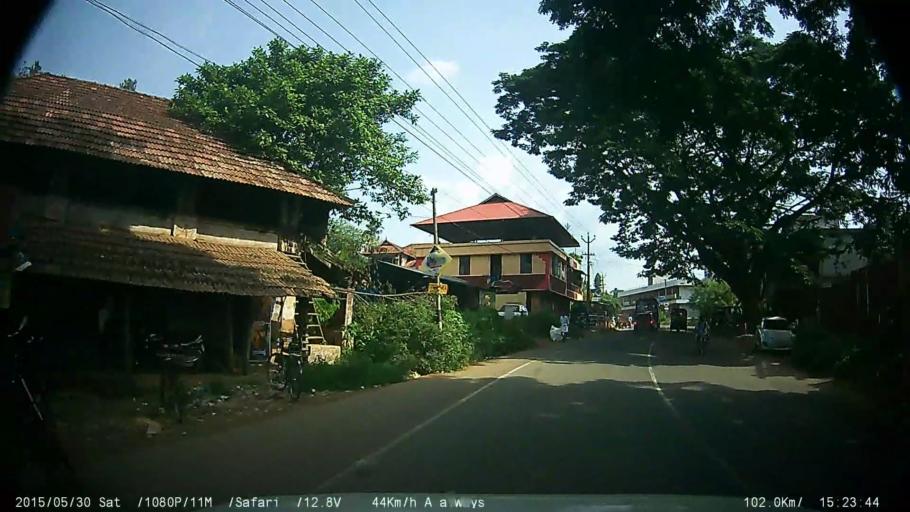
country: IN
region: Kerala
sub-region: Wayanad
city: Panamaram
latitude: 11.7353
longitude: 76.0732
